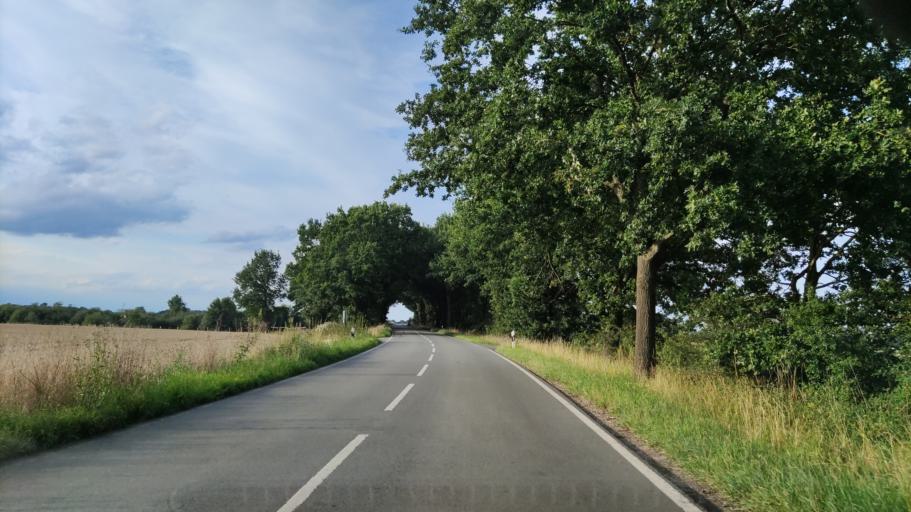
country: DE
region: Lower Saxony
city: Dannenberg
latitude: 53.1258
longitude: 11.1173
